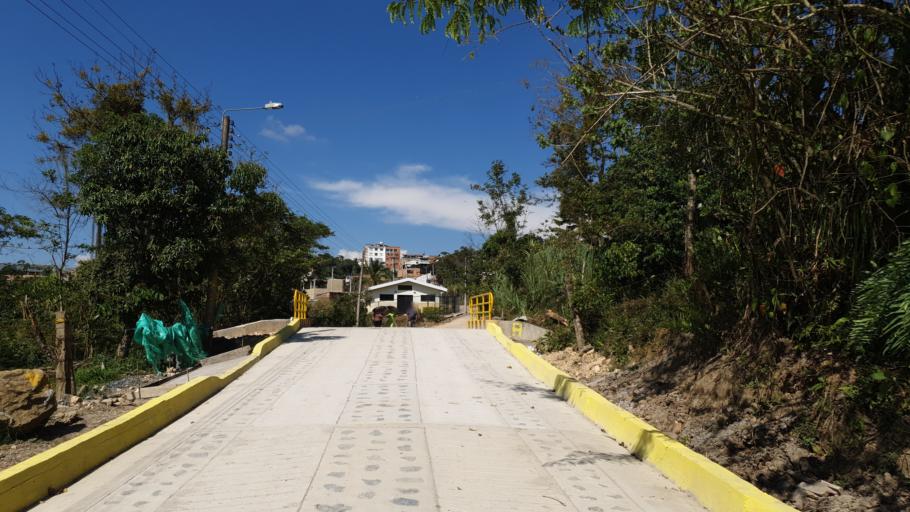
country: CO
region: Boyaca
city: Santana
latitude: 6.0546
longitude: -73.4855
